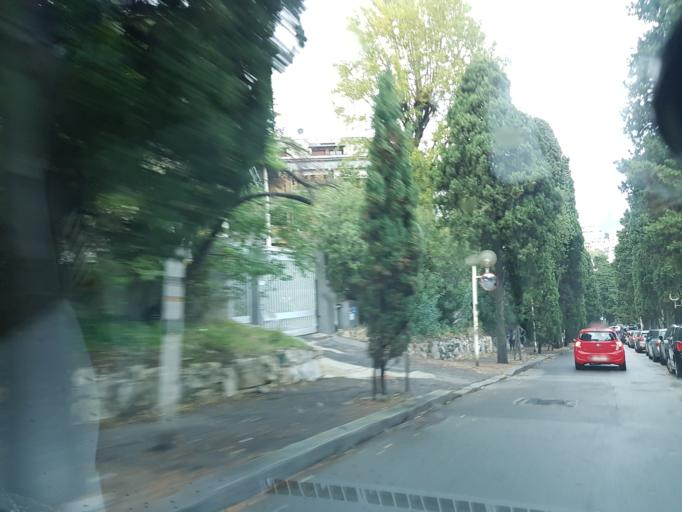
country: IT
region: Liguria
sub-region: Provincia di Genova
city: Genoa
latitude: 44.3997
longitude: 8.9700
